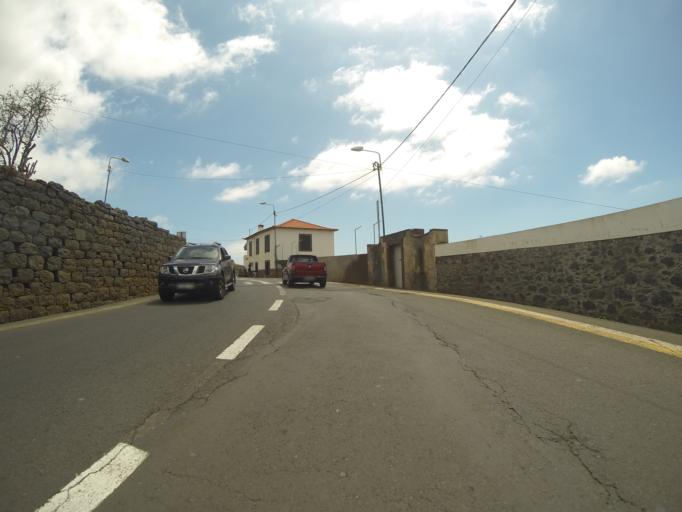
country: PT
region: Madeira
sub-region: Funchal
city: Nossa Senhora do Monte
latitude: 32.6649
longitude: -16.9322
